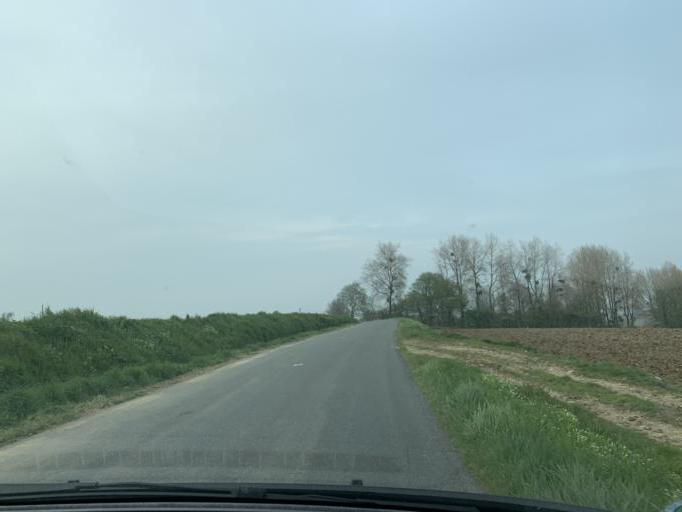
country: FR
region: Nord-Pas-de-Calais
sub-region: Departement du Pas-de-Calais
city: Longfosse
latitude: 50.6902
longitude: 1.7698
